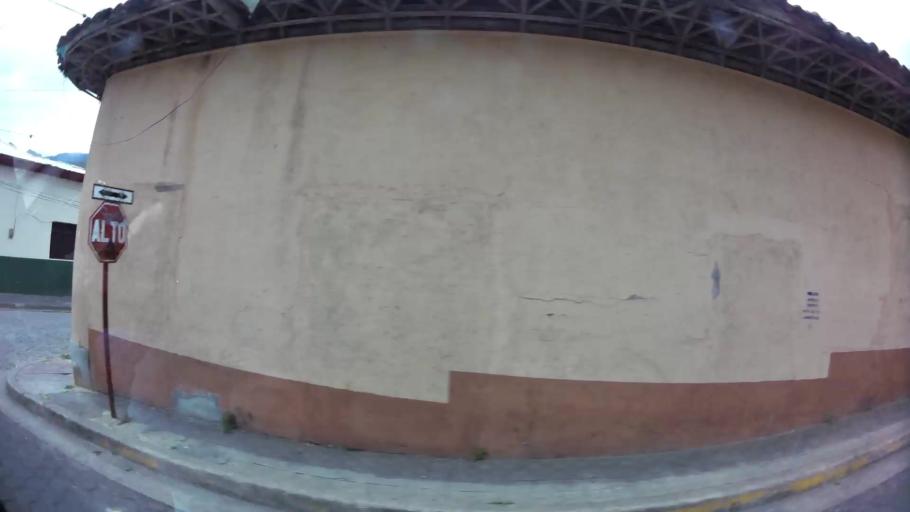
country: NI
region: Matagalpa
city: Matagalpa
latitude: 12.9300
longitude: -85.9135
